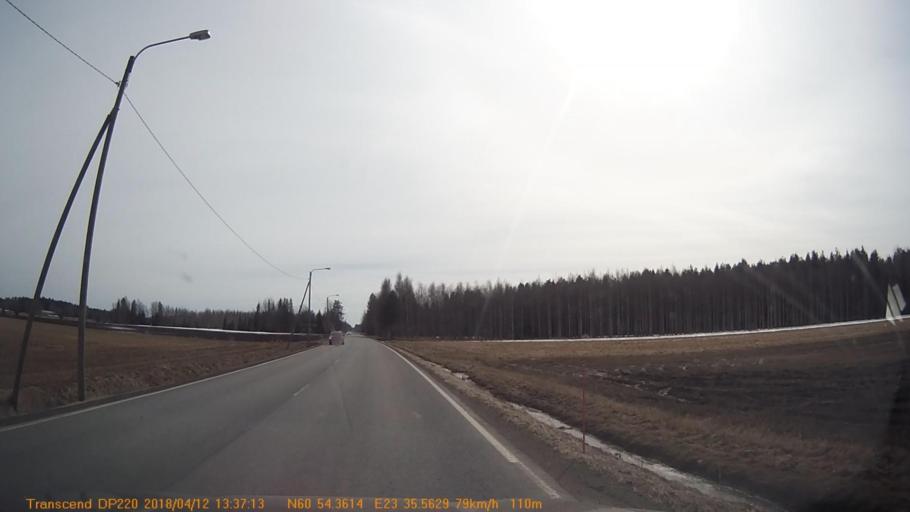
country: FI
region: Haeme
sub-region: Forssa
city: Forssa
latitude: 60.9058
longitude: 23.5928
